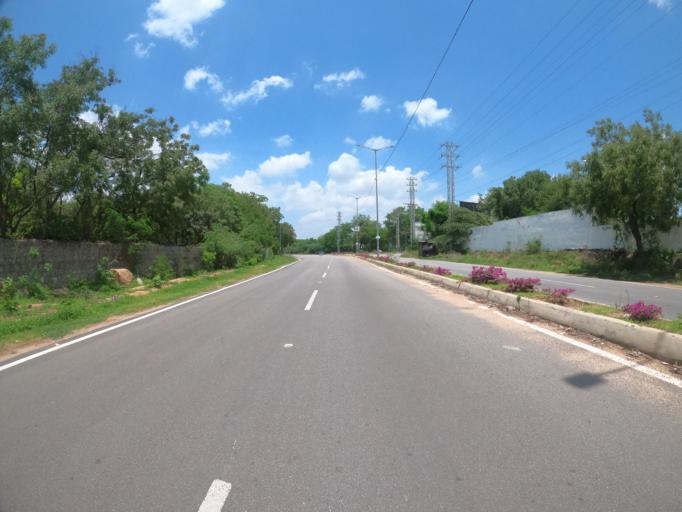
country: IN
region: Telangana
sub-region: Rangareddi
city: Sriramnagar
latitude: 17.3538
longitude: 78.3303
